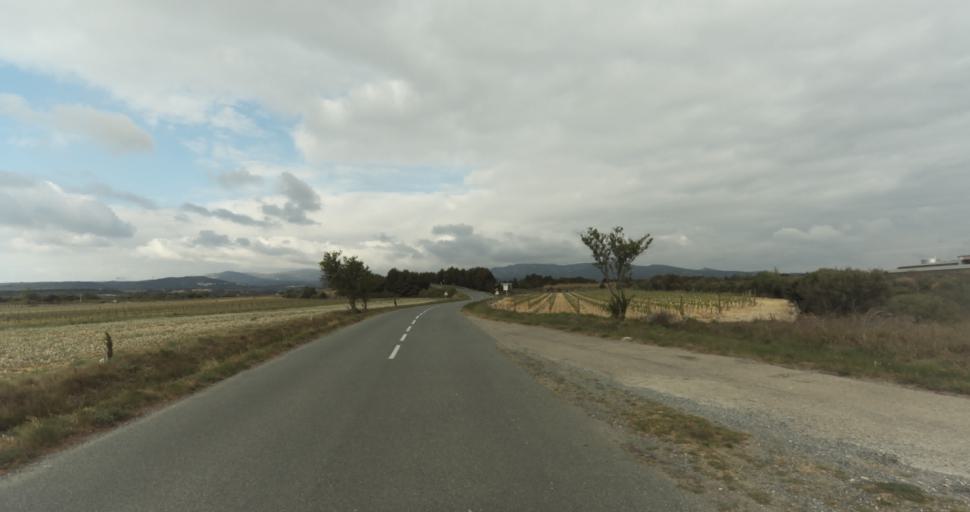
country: FR
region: Languedoc-Roussillon
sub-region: Departement de l'Aude
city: Leucate
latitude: 42.9317
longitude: 2.9968
